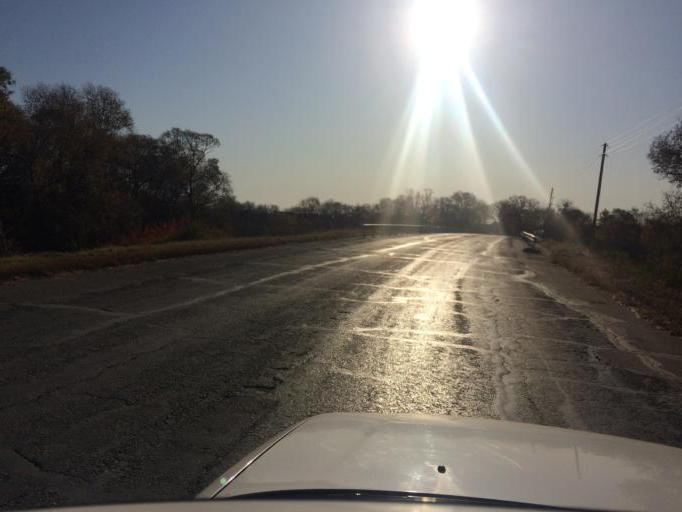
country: RU
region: Primorskiy
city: Dal'nerechensk
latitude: 45.9146
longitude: 133.7886
